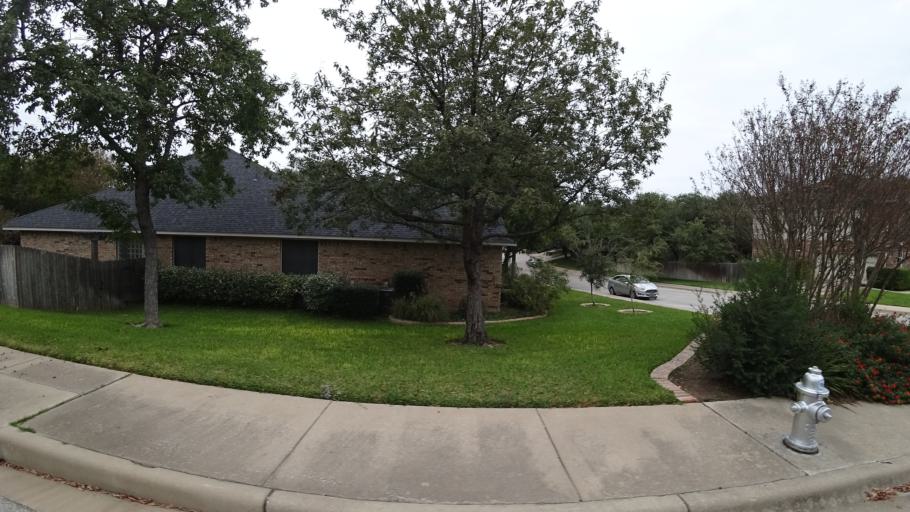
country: US
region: Texas
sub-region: Travis County
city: Bee Cave
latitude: 30.3167
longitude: -97.9195
